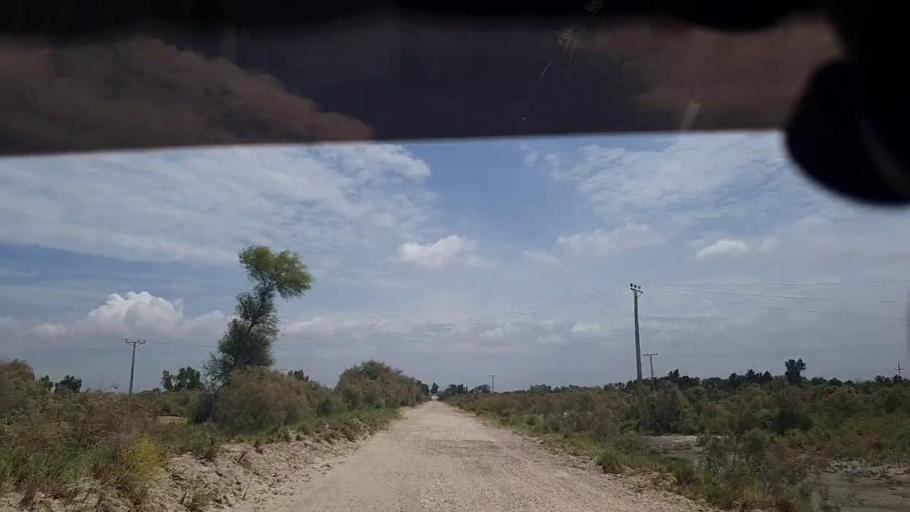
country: PK
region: Sindh
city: Rustam jo Goth
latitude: 28.0255
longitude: 68.9388
